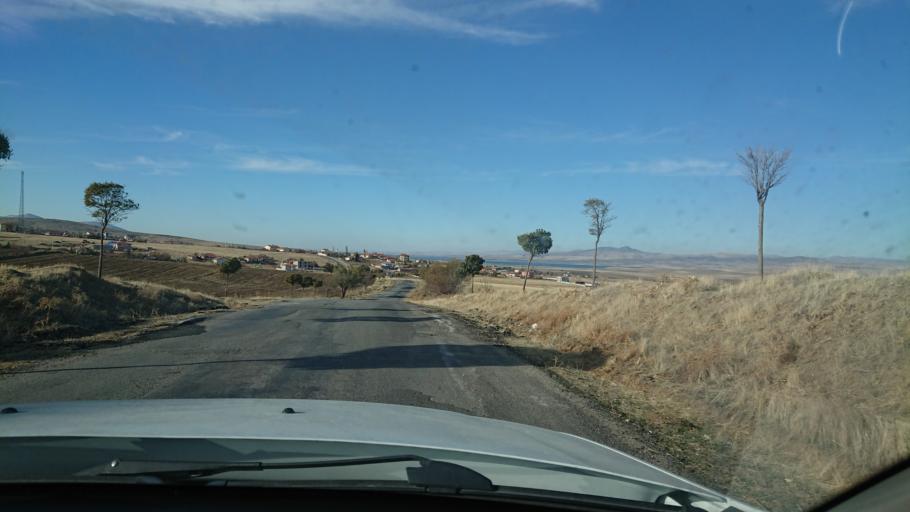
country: TR
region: Aksaray
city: Sariyahsi
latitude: 38.9739
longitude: 33.8590
